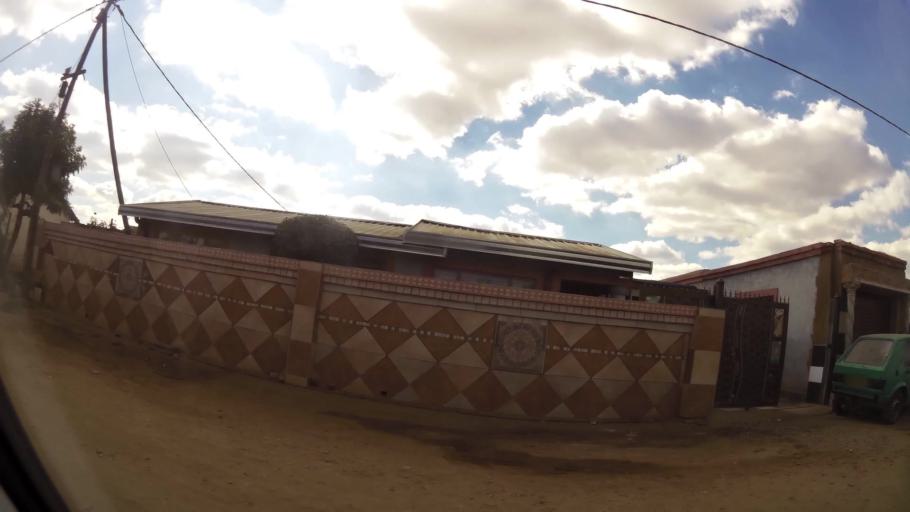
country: ZA
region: Gauteng
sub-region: City of Tshwane Metropolitan Municipality
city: Cullinan
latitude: -25.7123
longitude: 28.4000
